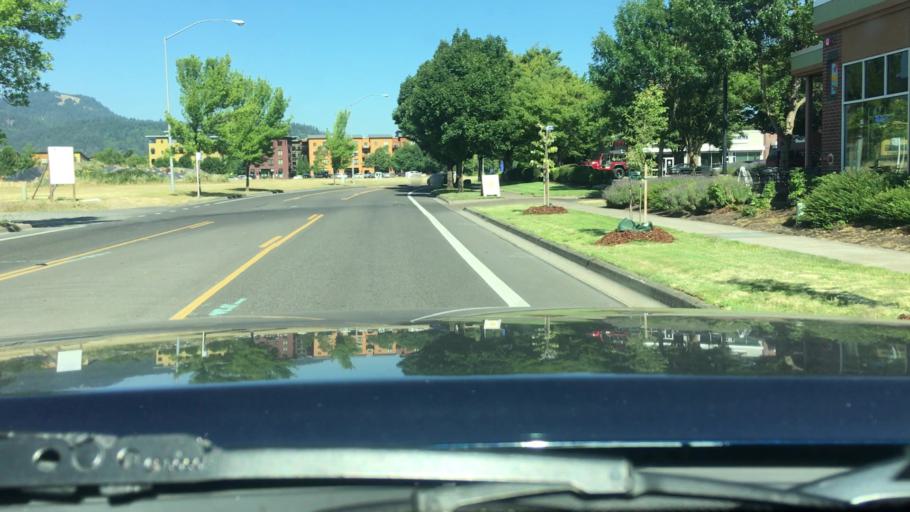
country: US
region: Oregon
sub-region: Lane County
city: Coburg
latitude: 44.0929
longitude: -123.0645
